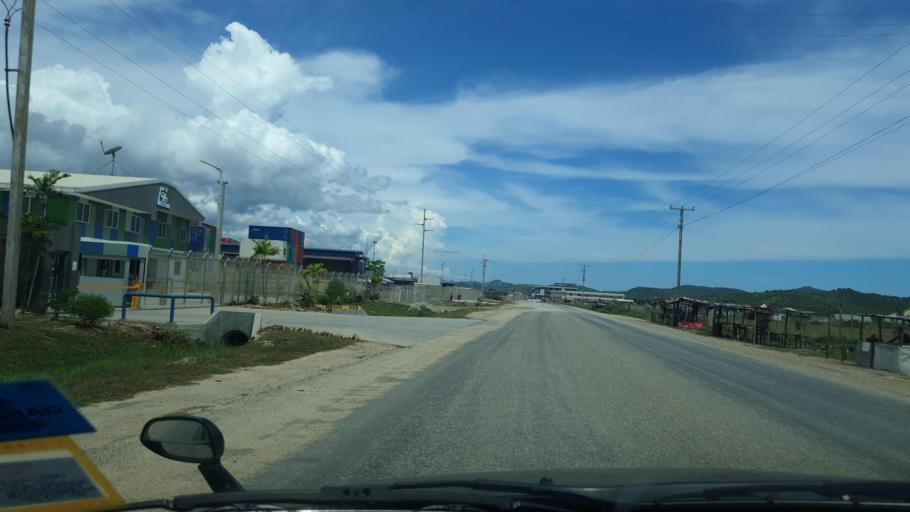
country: PG
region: National Capital
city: Port Moresby
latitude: -9.4164
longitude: 147.0744
